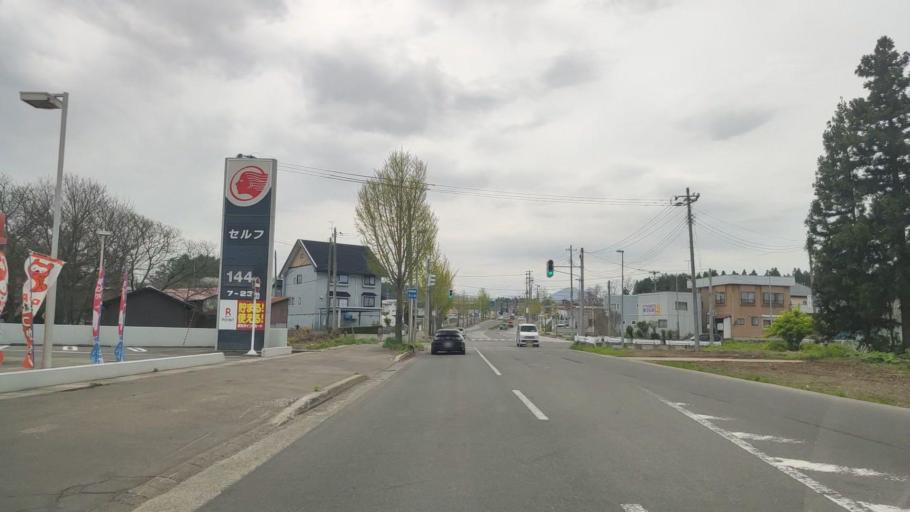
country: JP
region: Aomori
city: Aomori Shi
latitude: 40.7927
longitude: 140.7862
